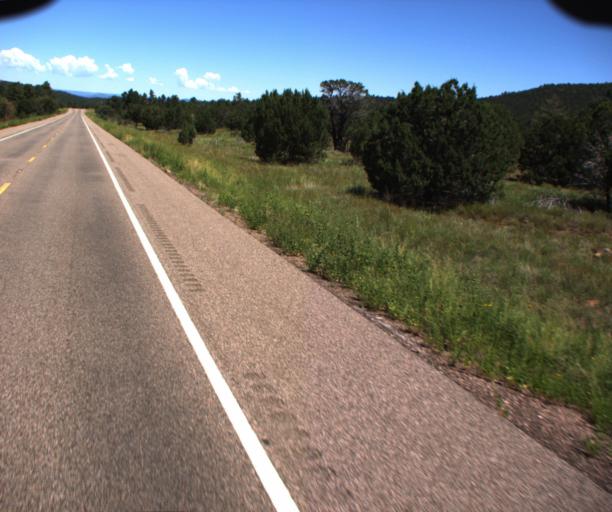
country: US
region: Arizona
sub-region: Gila County
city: San Carlos
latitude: 33.6668
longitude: -110.5723
